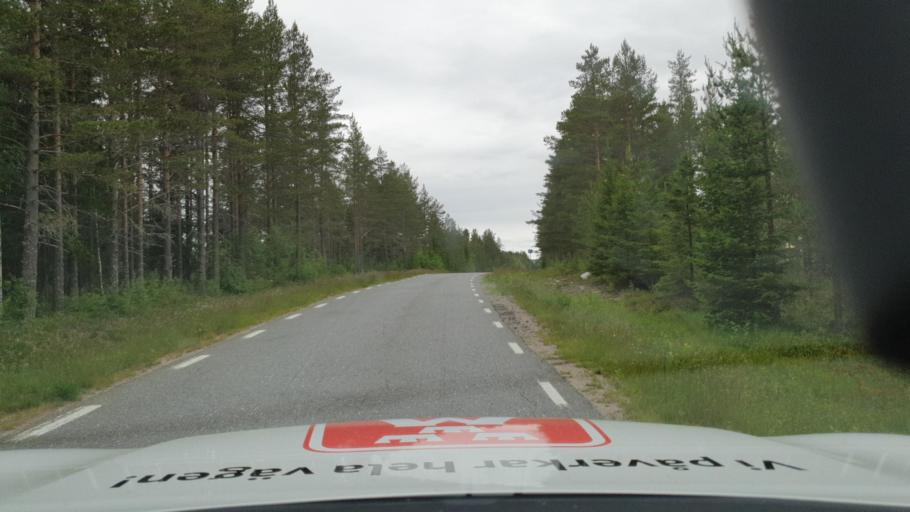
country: SE
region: Vaesterbotten
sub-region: Nordmalings Kommun
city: Nordmaling
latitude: 63.4874
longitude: 19.4407
